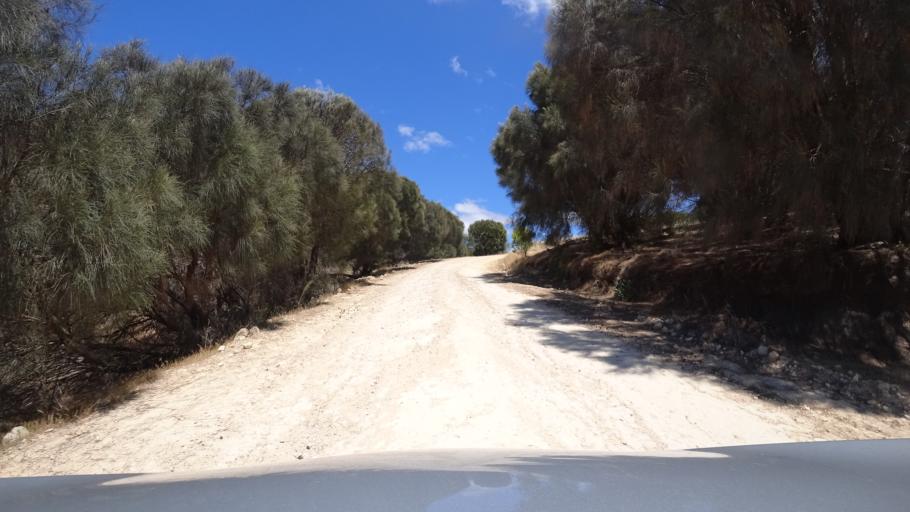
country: AU
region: South Australia
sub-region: Yankalilla
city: Normanville
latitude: -35.7830
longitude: 138.0661
